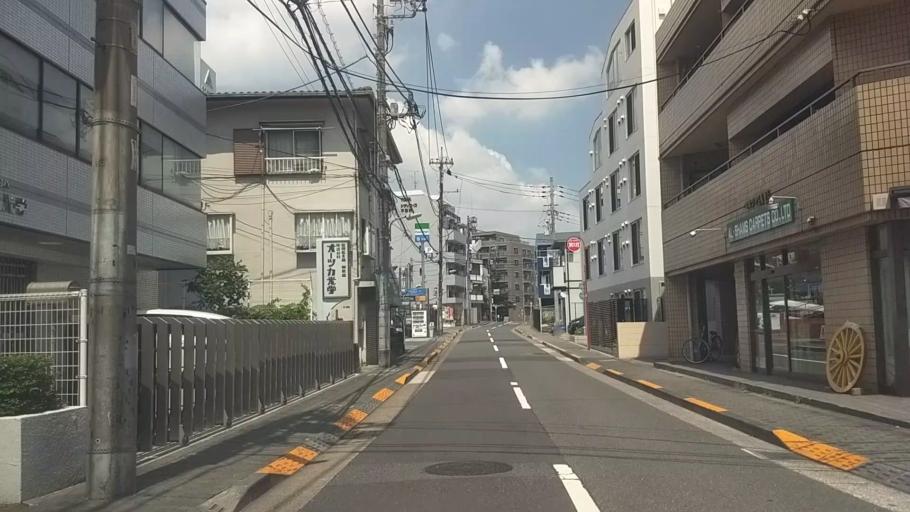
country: JP
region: Tokyo
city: Tokyo
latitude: 35.6235
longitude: 139.7113
